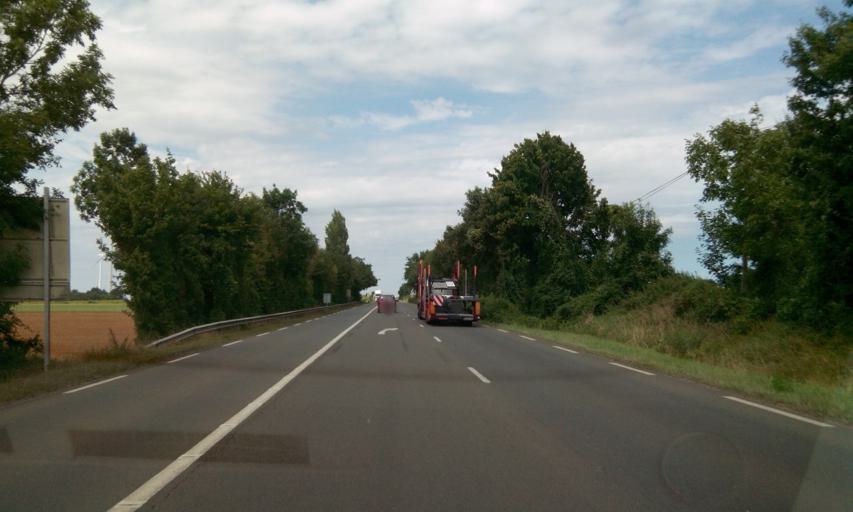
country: FR
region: Poitou-Charentes
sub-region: Departement des Deux-Sevres
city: Melle
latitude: 46.2303
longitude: -0.1629
